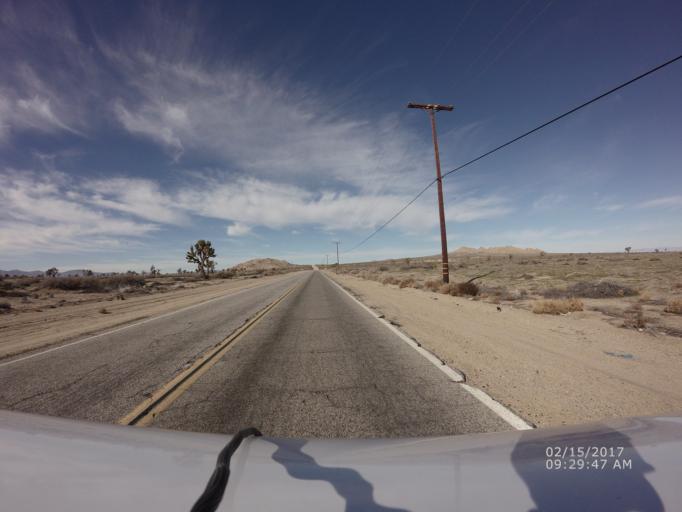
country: US
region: California
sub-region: Los Angeles County
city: Lake Los Angeles
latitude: 34.6166
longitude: -117.8677
